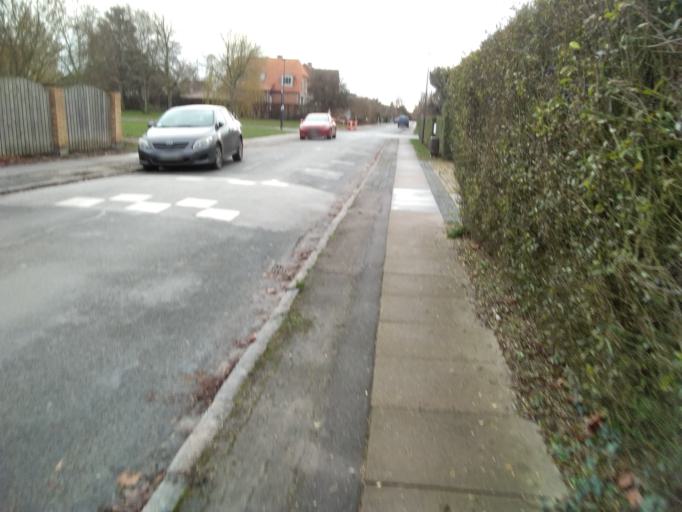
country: DK
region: Capital Region
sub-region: Tarnby Kommune
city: Tarnby
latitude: 55.6436
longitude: 12.6184
